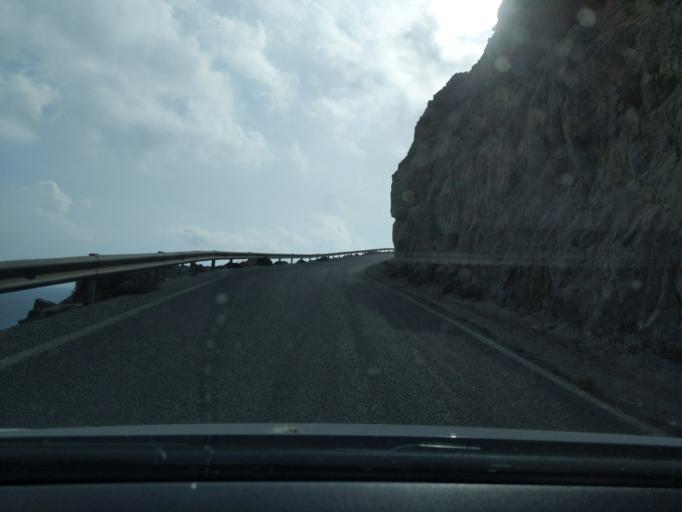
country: GR
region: Crete
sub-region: Nomos Lasithiou
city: Palekastro
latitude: 35.0893
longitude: 26.2661
